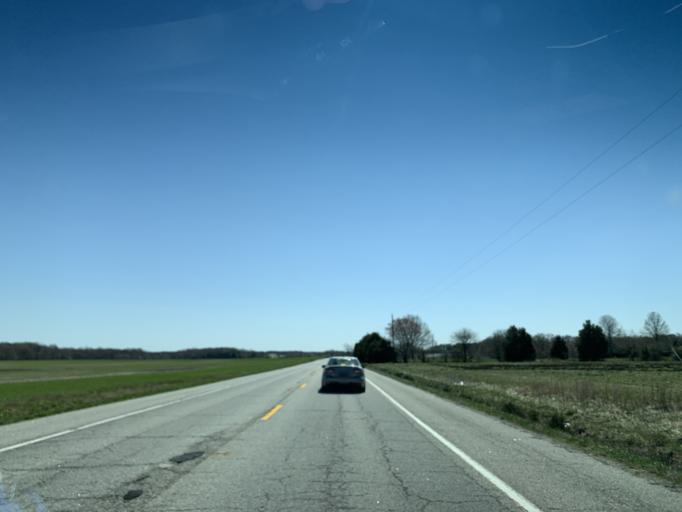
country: US
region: Maryland
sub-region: Queen Anne's County
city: Centreville
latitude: 38.9875
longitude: -76.0248
